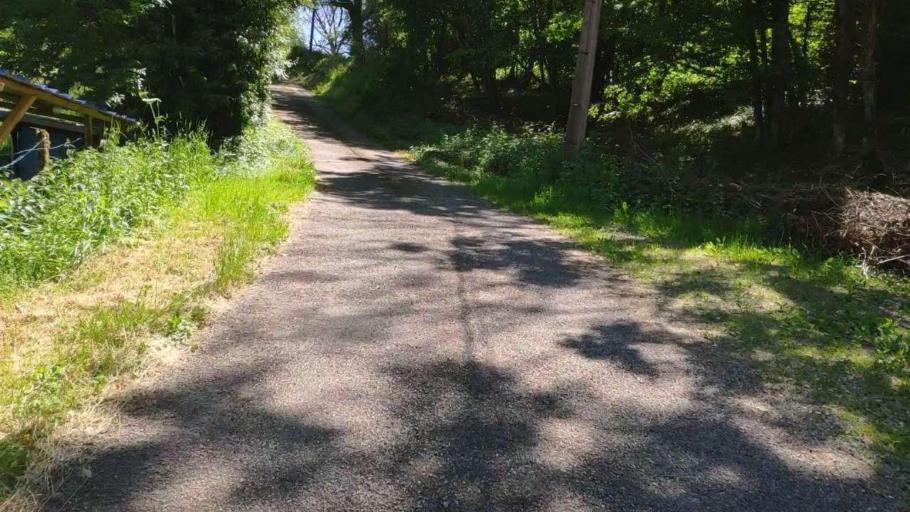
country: FR
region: Franche-Comte
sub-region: Departement du Jura
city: Perrigny
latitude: 46.7322
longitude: 5.6297
